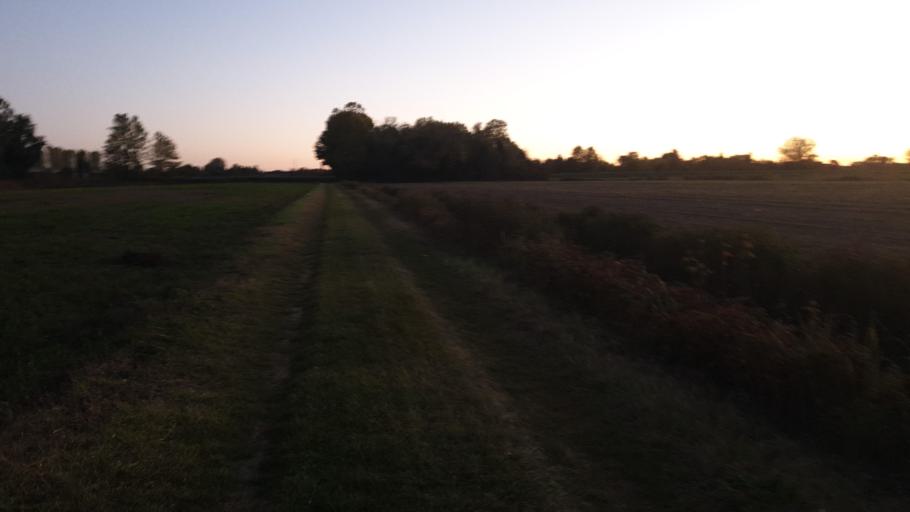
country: IT
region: Veneto
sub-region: Provincia di Venezia
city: Fiesso d'Artico
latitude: 45.4309
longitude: 12.0321
